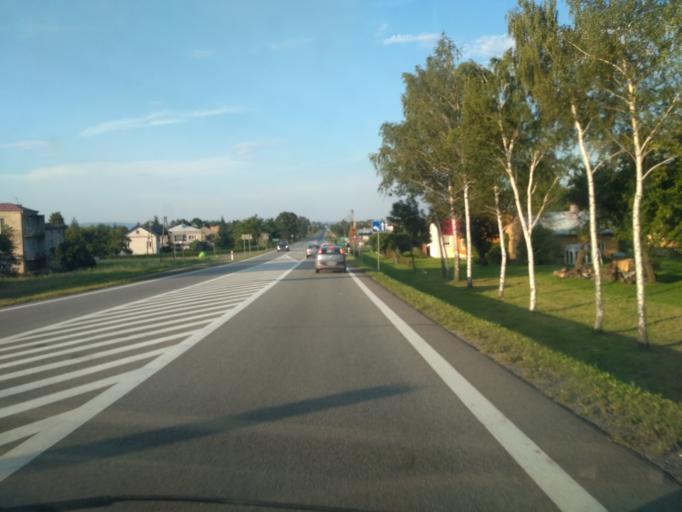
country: PL
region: Subcarpathian Voivodeship
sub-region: Powiat krosnienski
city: Miejsce Piastowe
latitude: 49.6137
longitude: 21.7491
